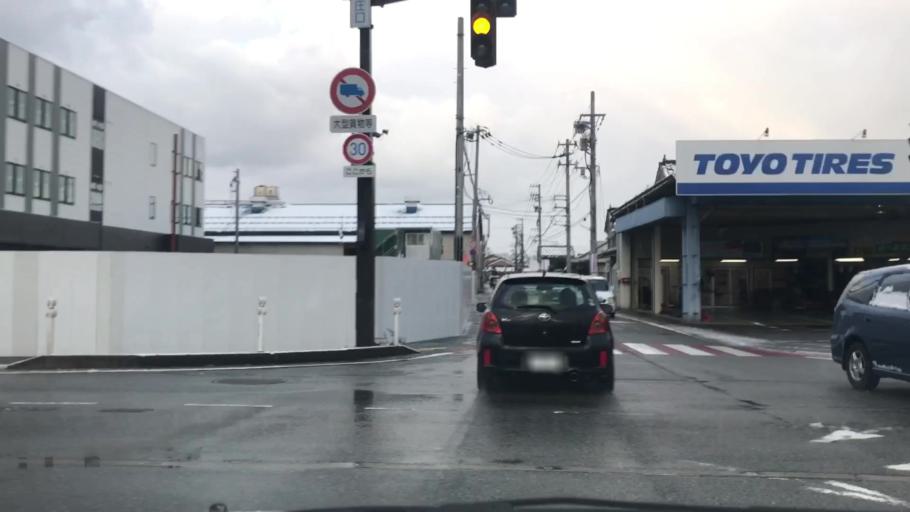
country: JP
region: Toyama
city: Toyama-shi
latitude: 36.7027
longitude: 137.2591
